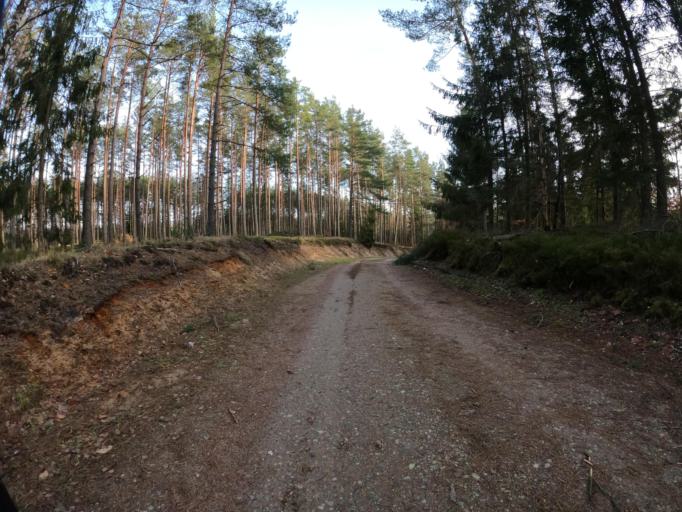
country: PL
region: West Pomeranian Voivodeship
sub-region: Powiat koszalinski
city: Polanow
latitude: 54.1539
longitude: 16.6719
